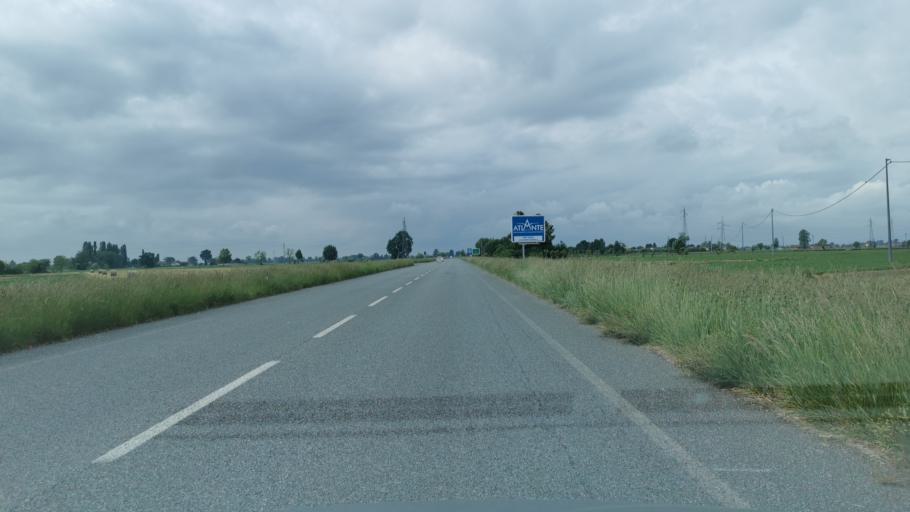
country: IT
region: Piedmont
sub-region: Provincia di Cuneo
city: Racconigi
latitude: 44.7724
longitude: 7.7003
